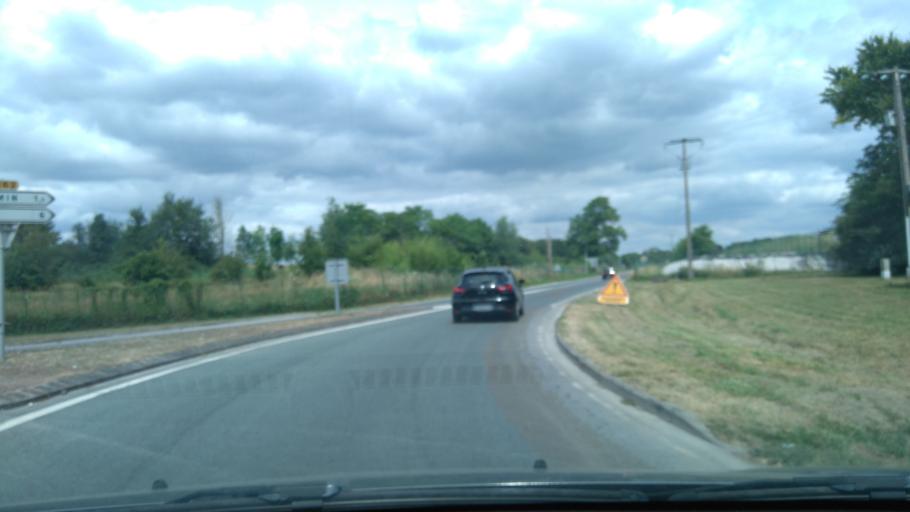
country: FR
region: Picardie
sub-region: Departement de l'Oise
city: Saint-Maximin
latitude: 49.2109
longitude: 2.4451
